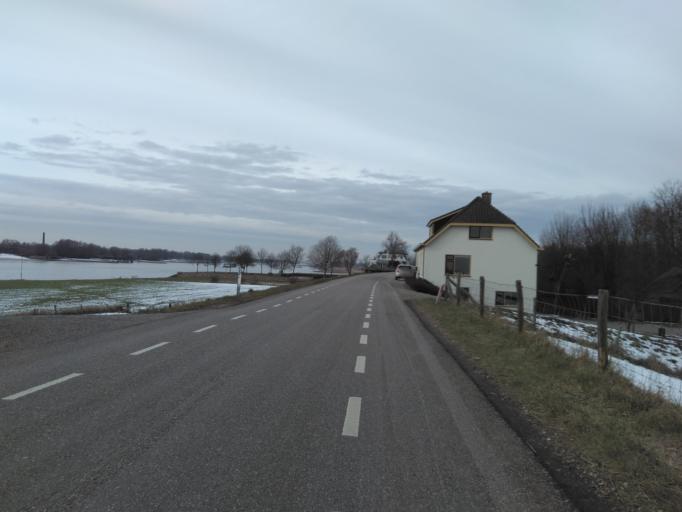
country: NL
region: Gelderland
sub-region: Gemeente Overbetuwe
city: Oosterhout
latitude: 51.8749
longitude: 5.8111
